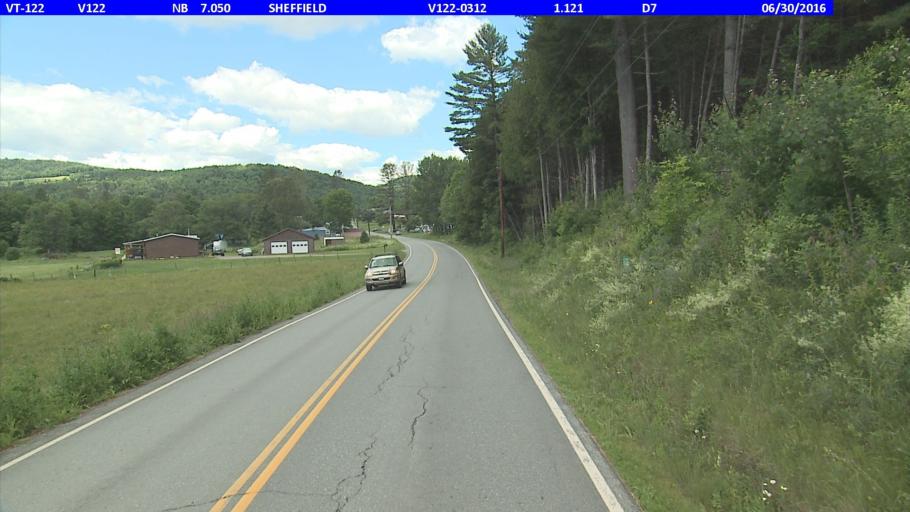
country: US
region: Vermont
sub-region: Caledonia County
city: Lyndonville
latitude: 44.5995
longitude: -72.1100
